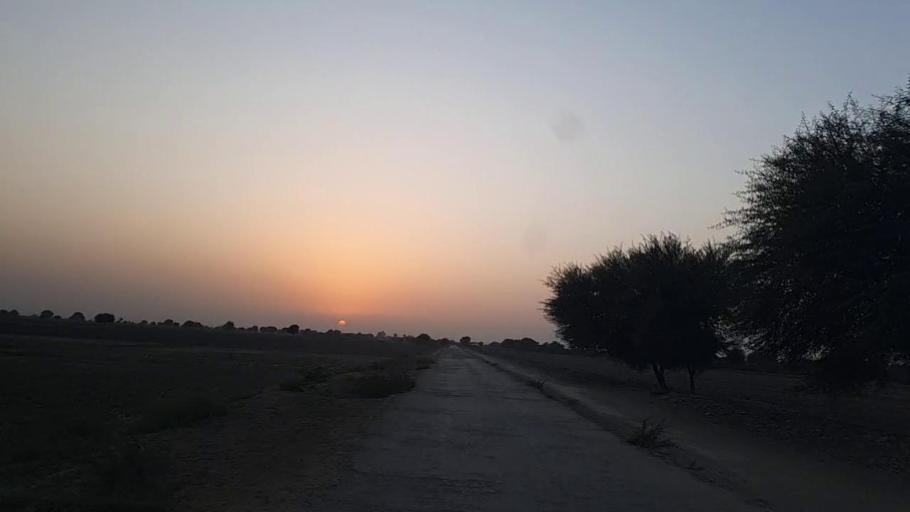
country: PK
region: Sindh
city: Naukot
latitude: 24.7483
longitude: 69.3242
